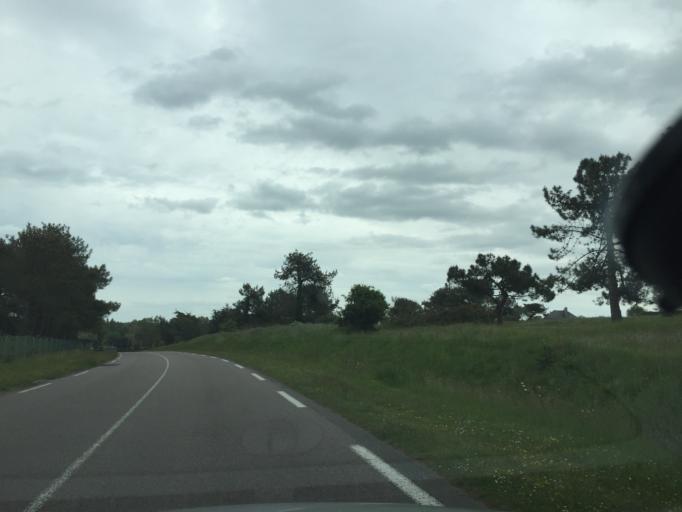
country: FR
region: Brittany
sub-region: Departement des Cotes-d'Armor
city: Plurien
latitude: 48.6519
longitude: -2.3612
